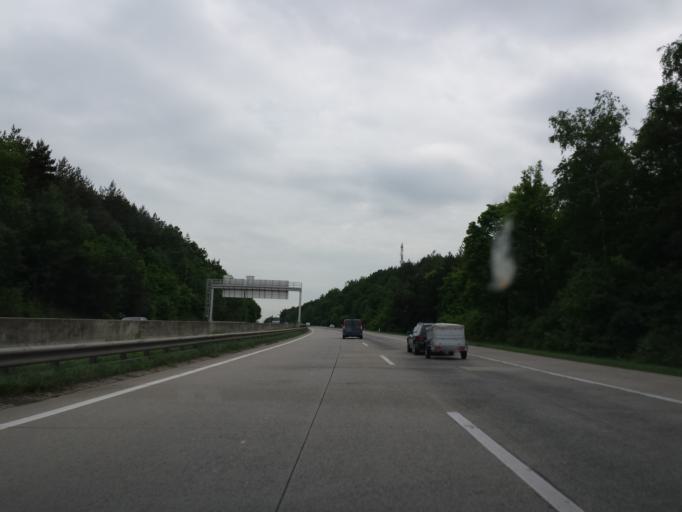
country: AT
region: Lower Austria
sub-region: Politischer Bezirk Neunkirchen
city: Seebenstein
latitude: 47.7079
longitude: 16.1291
